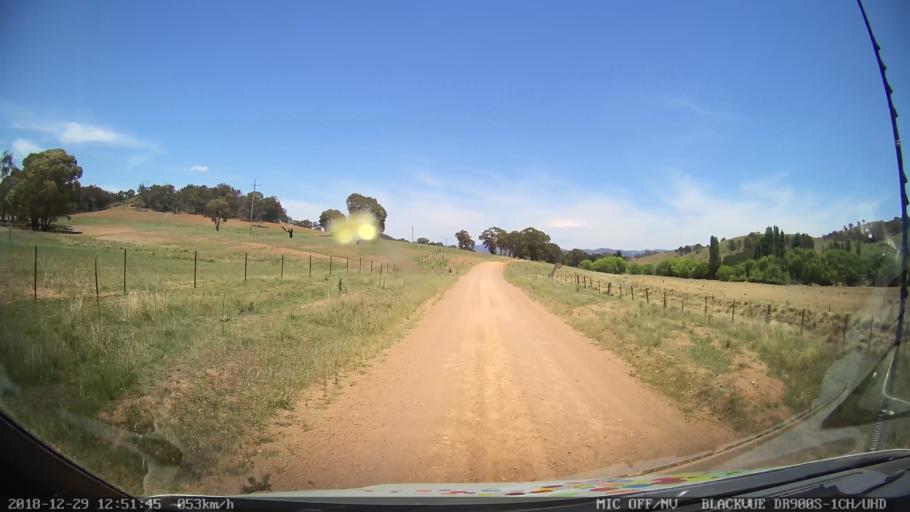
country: AU
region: Australian Capital Territory
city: Macarthur
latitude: -35.6769
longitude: 149.1973
